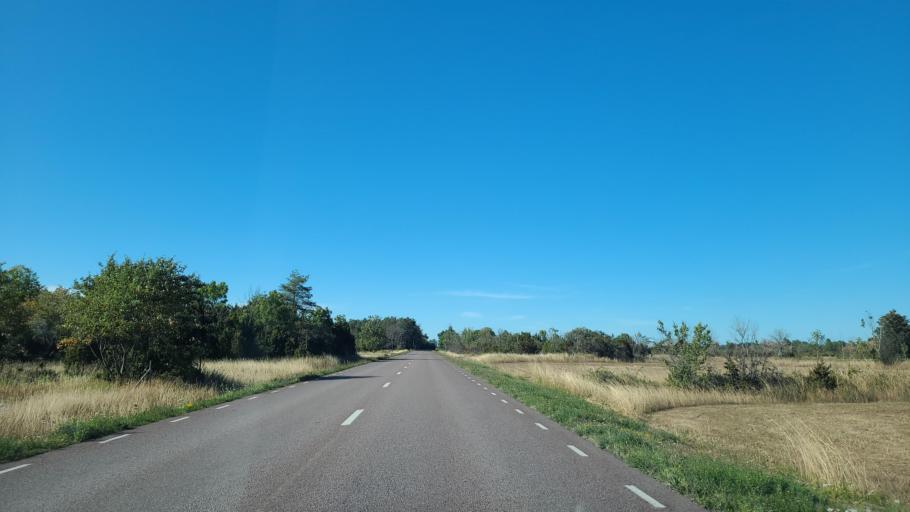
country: SE
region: Kalmar
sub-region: Borgholms Kommun
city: Borgholm
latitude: 57.2053
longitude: 17.0452
